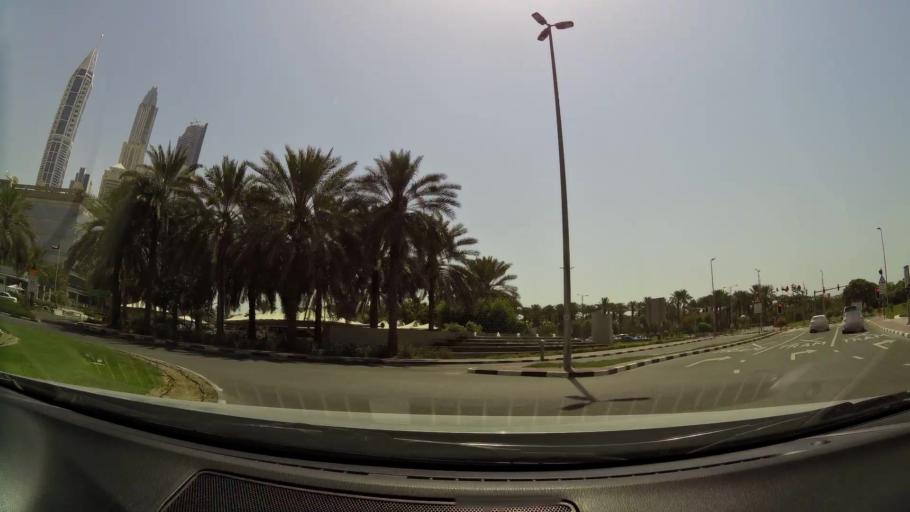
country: AE
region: Dubai
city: Dubai
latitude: 25.0950
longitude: 55.1532
